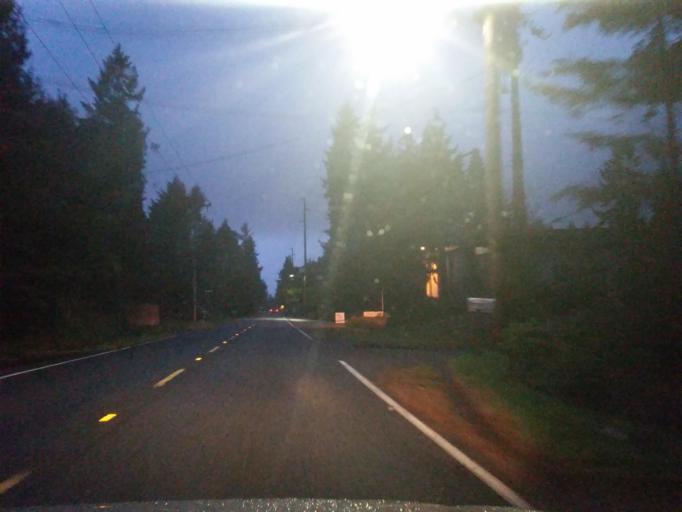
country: US
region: Washington
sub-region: King County
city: Shoreline
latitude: 47.7666
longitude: -122.3243
